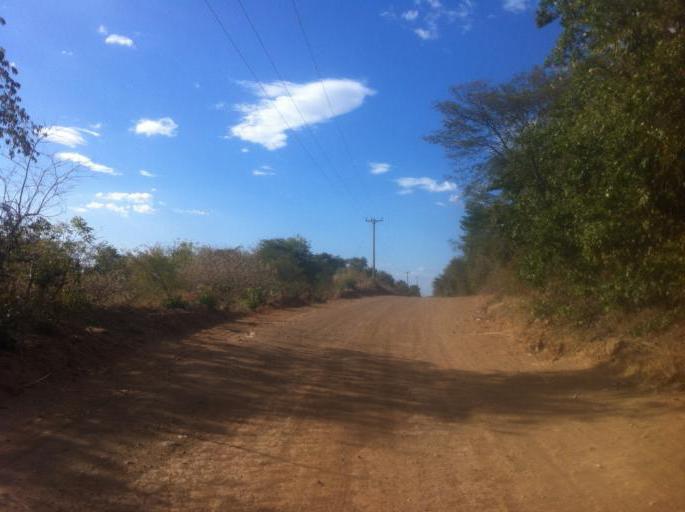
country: NI
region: Managua
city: Masachapa
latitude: 11.8134
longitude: -86.4961
